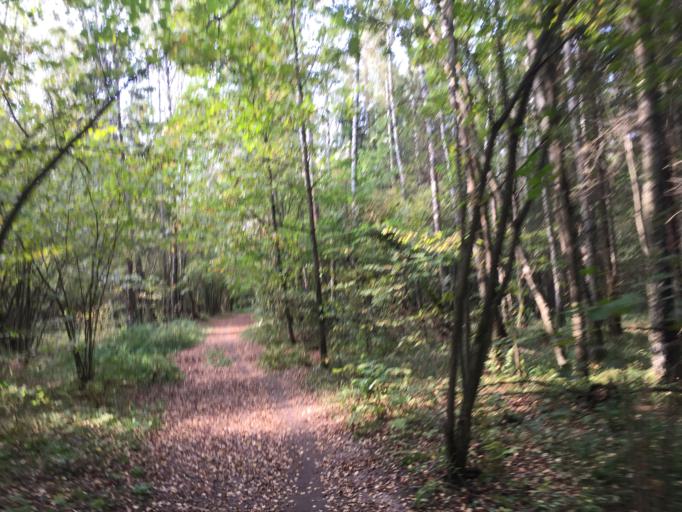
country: RU
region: Moscow
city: Babushkin
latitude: 55.8686
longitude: 37.7377
